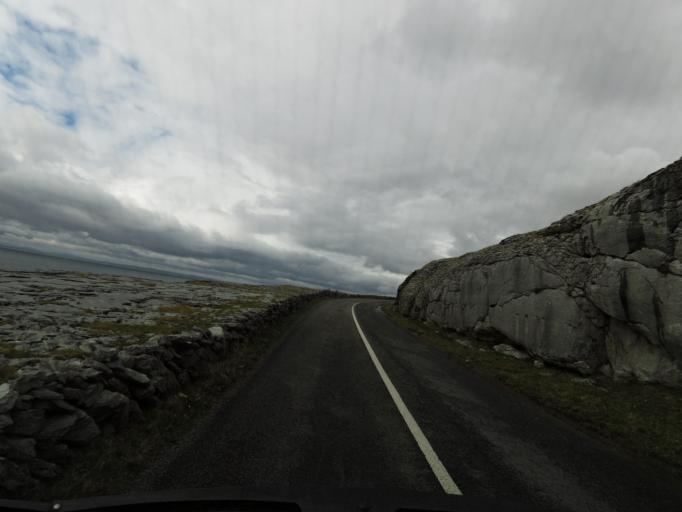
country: IE
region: Connaught
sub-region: County Galway
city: Bearna
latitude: 53.0706
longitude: -9.3575
